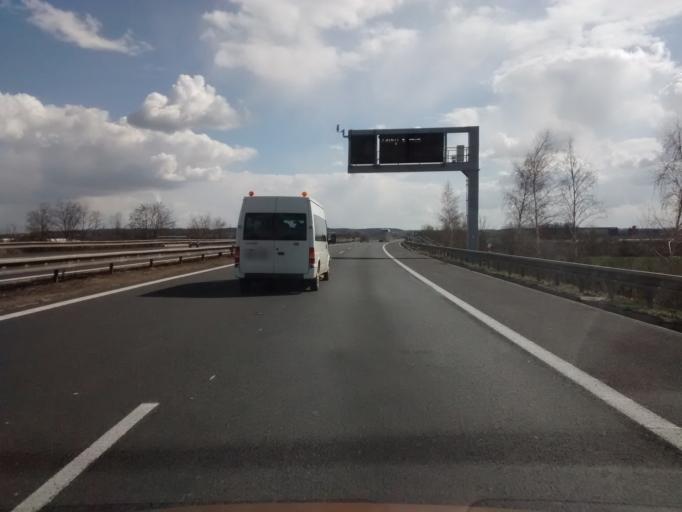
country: CZ
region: Central Bohemia
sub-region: Okres Melnik
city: Veltrusy
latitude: 50.2617
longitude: 14.3686
